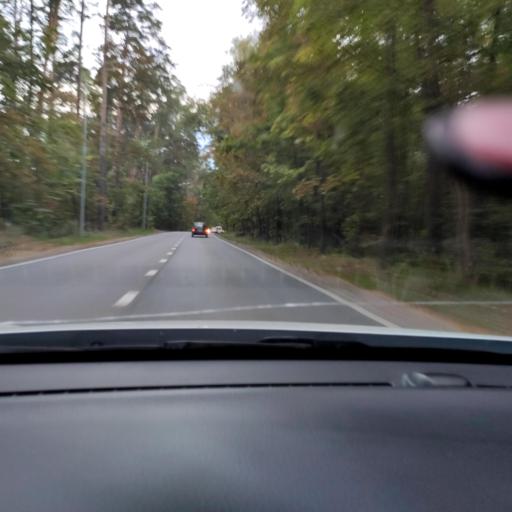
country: RU
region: Mariy-El
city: Volzhsk
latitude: 55.8405
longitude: 48.4343
